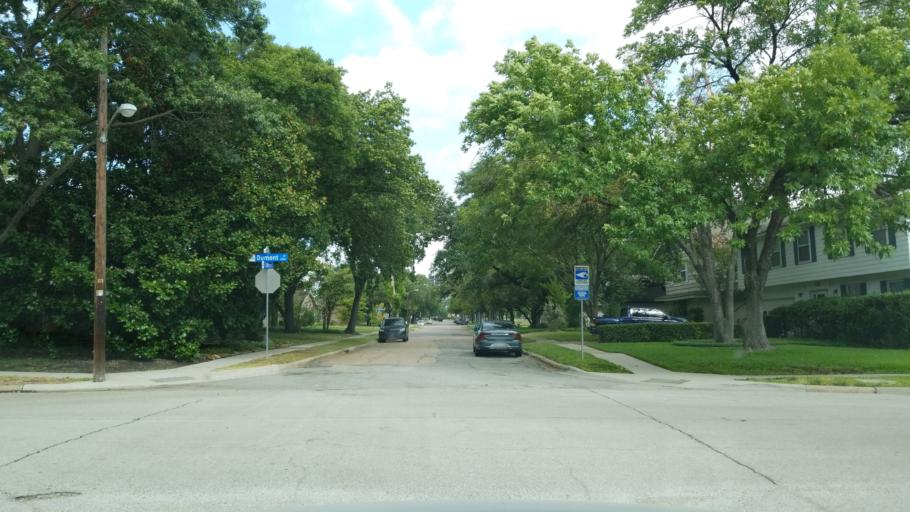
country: US
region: Texas
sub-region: Dallas County
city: Richardson
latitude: 32.9465
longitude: -96.7655
